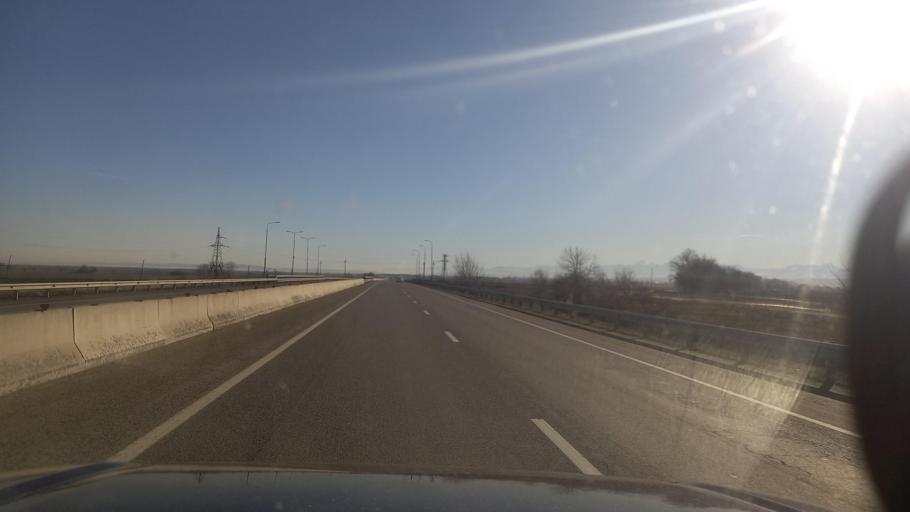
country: RU
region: Kabardino-Balkariya
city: Kishpek
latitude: 43.5890
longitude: 43.6787
